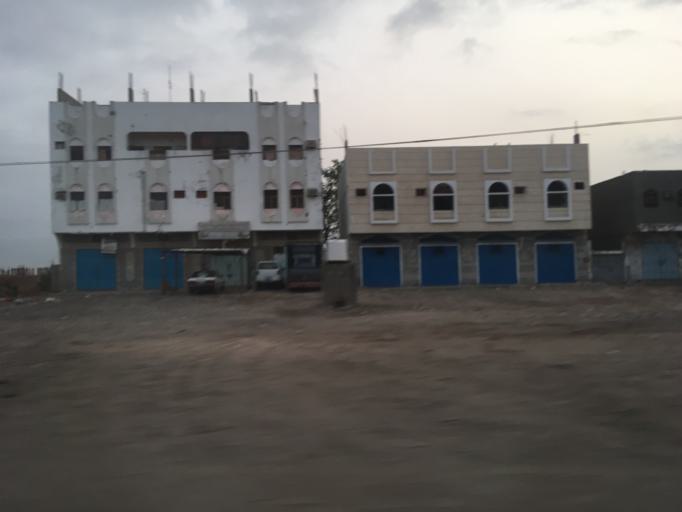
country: YE
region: Lahij
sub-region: Al  Hawtah
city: Lahij
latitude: 13.0080
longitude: 44.9088
